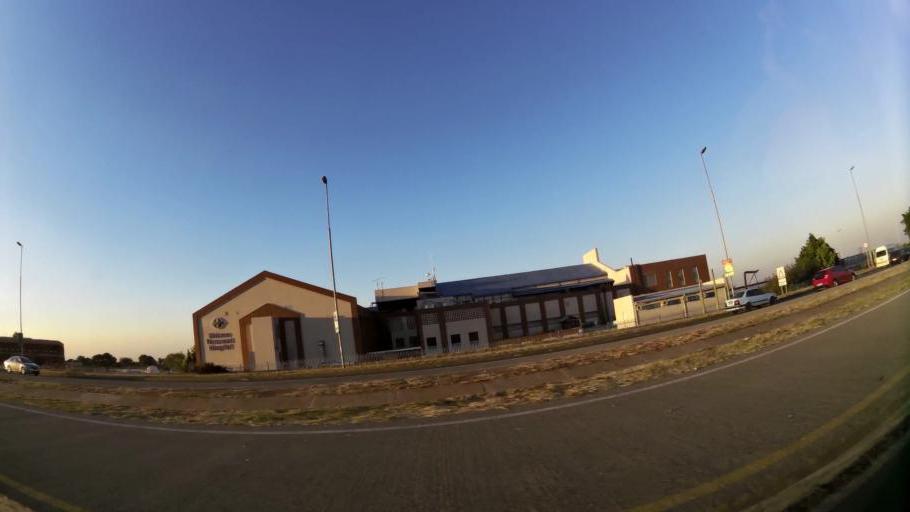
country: ZA
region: North-West
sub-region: Bojanala Platinum District Municipality
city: Rustenburg
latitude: -25.6486
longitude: 27.2131
